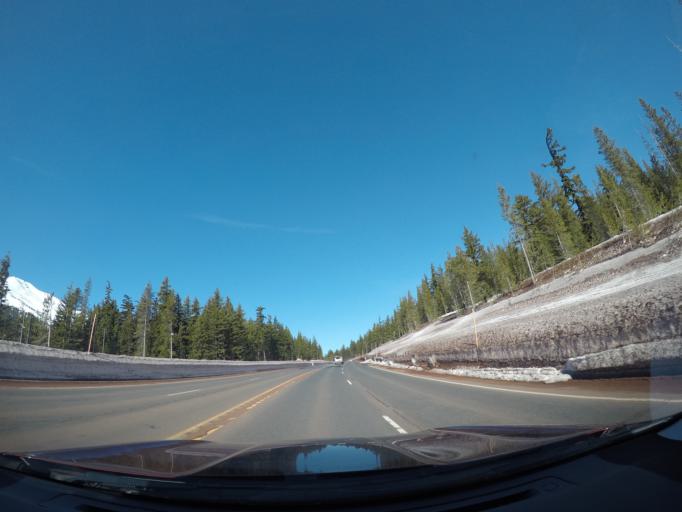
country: US
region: Oregon
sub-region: Deschutes County
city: Sunriver
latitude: 43.9874
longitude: -121.6479
